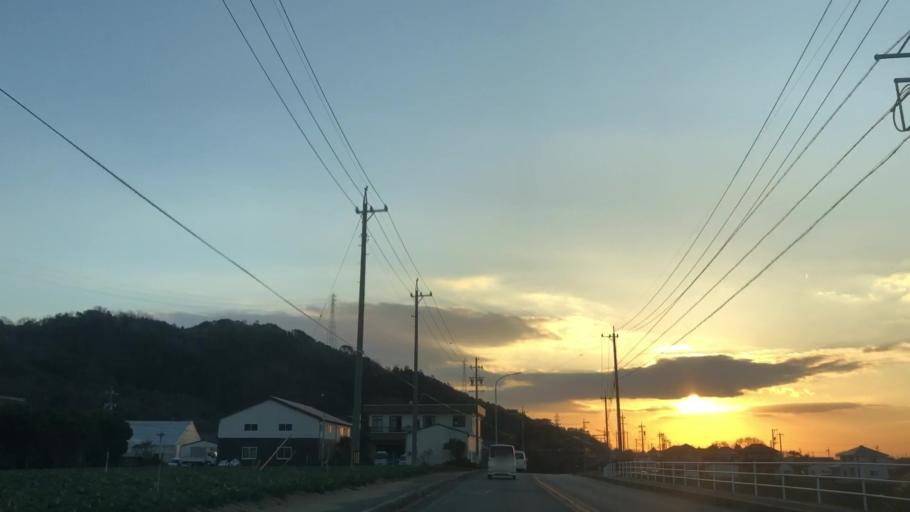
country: JP
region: Aichi
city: Toyohama
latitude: 34.6063
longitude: 137.0666
